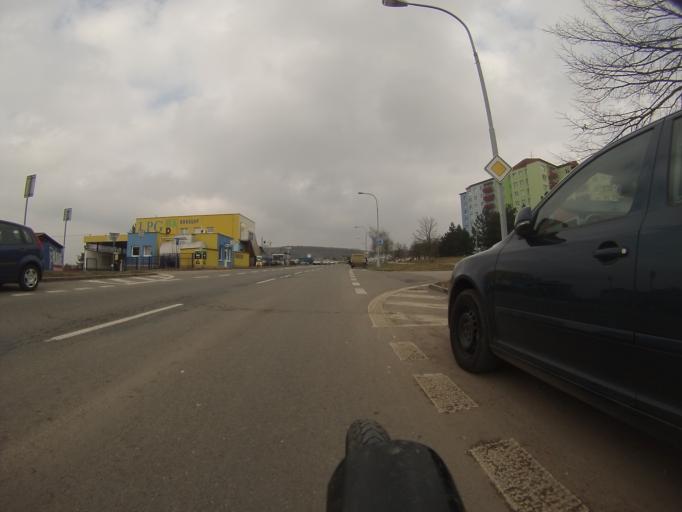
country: CZ
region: South Moravian
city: Bilovice nad Svitavou
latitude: 49.2088
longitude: 16.6737
